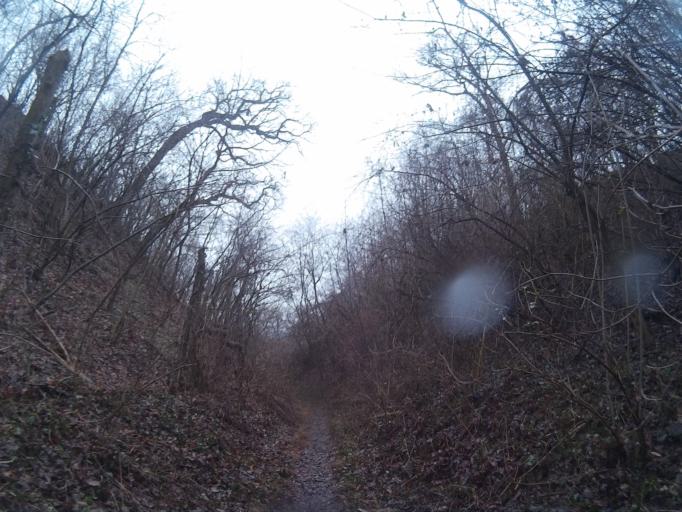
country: HU
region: Komarom-Esztergom
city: Nyergesujfalu
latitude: 47.7118
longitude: 18.5830
